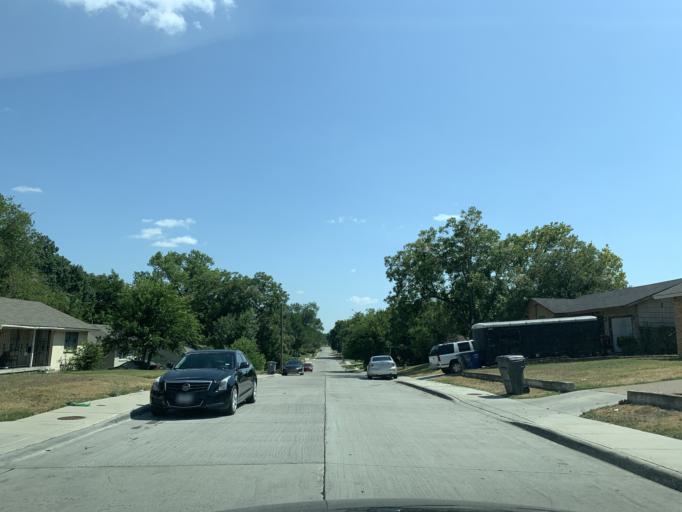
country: US
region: Texas
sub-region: Dallas County
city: Hutchins
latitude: 32.6774
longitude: -96.7935
